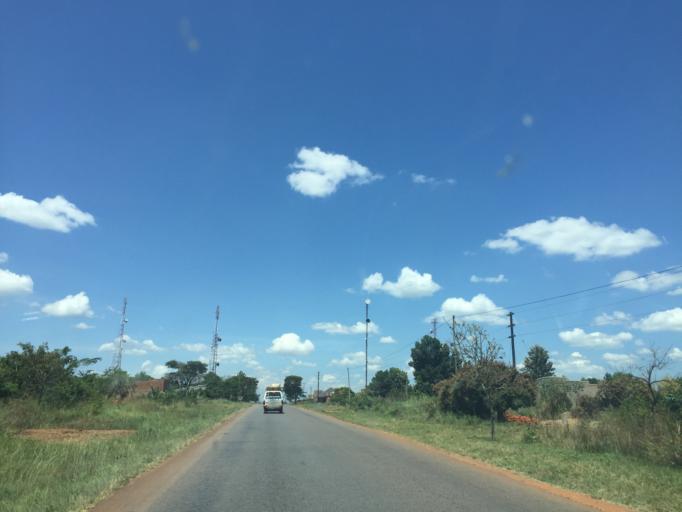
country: UG
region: Western Region
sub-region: Kiryandongo District
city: Masindi Port
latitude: 1.5063
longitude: 32.1022
